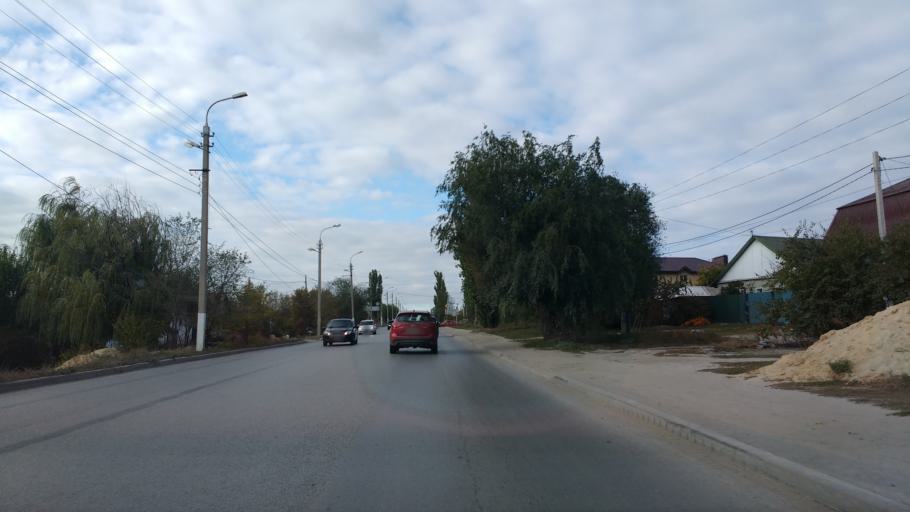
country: RU
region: Volgograd
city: Volgograd
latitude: 48.7631
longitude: 44.5327
